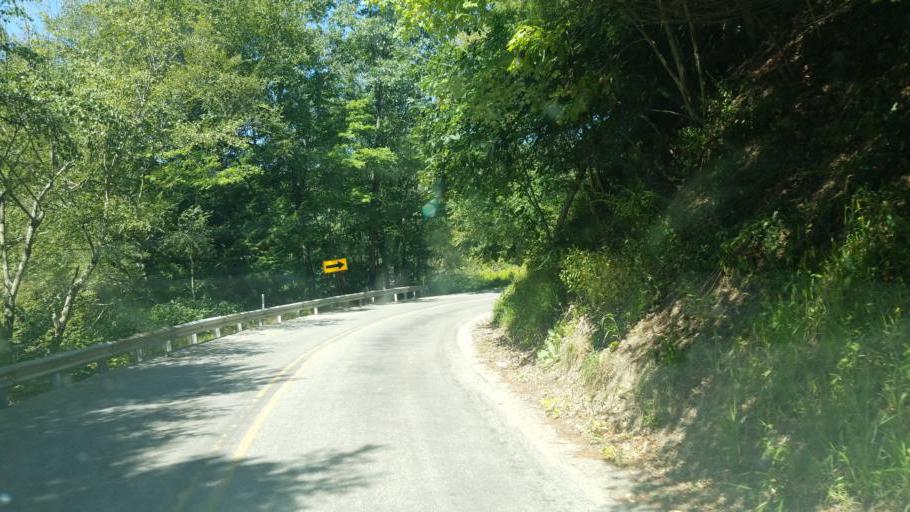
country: US
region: Pennsylvania
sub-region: Clarion County
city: Knox
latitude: 41.1703
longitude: -79.4777
